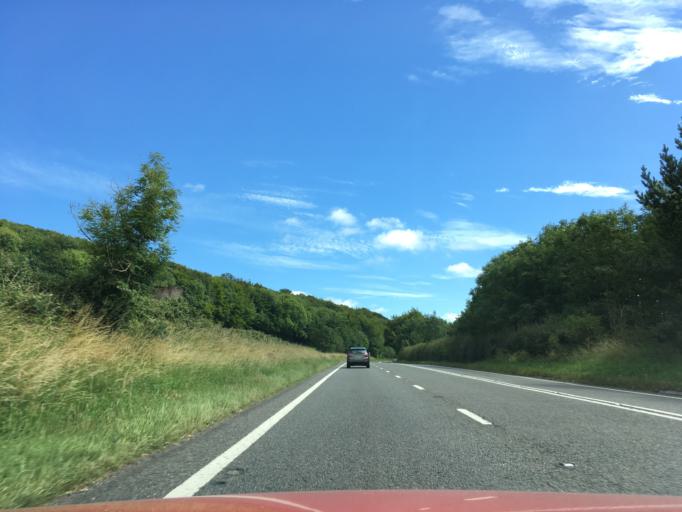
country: GB
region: England
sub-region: Somerset
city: Yeovil
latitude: 50.8536
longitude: -2.5856
